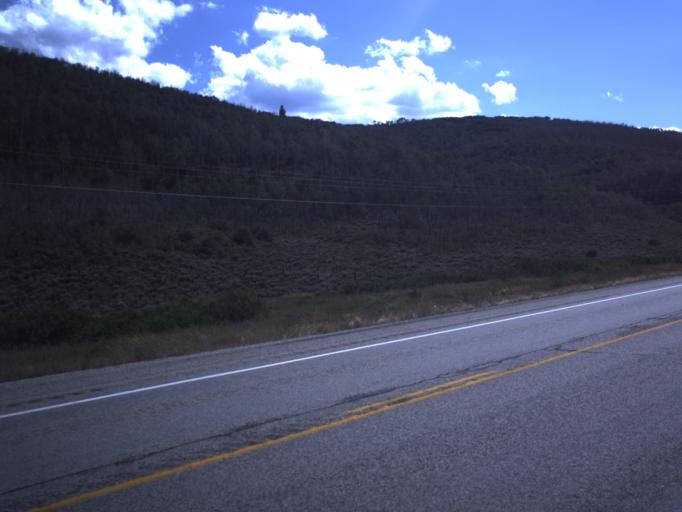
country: US
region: Utah
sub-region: Summit County
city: Francis
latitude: 40.2023
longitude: -110.9849
